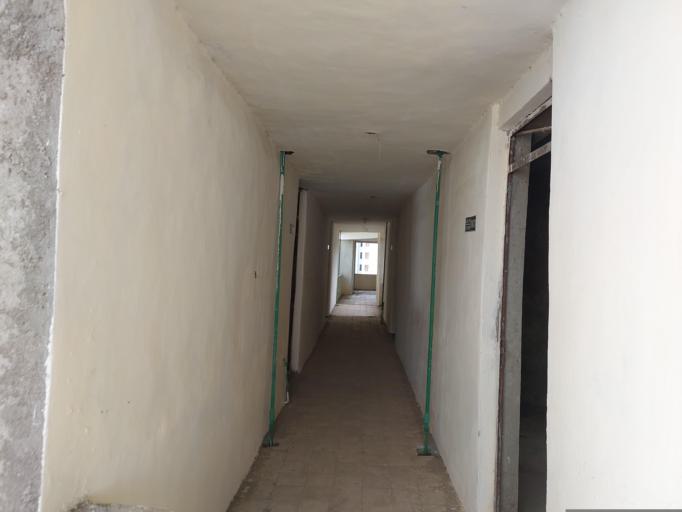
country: ET
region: Adis Abeba
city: Addis Ababa
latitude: 8.9618
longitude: 38.8753
